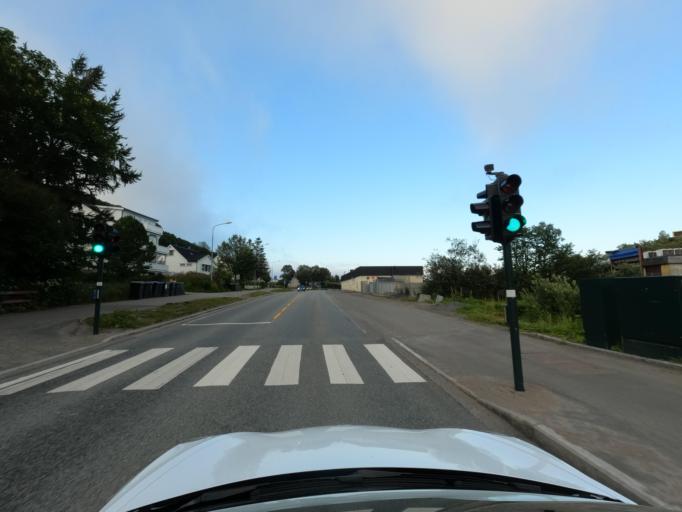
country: NO
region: Troms
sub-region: Harstad
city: Harstad
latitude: 68.8056
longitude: 16.5230
